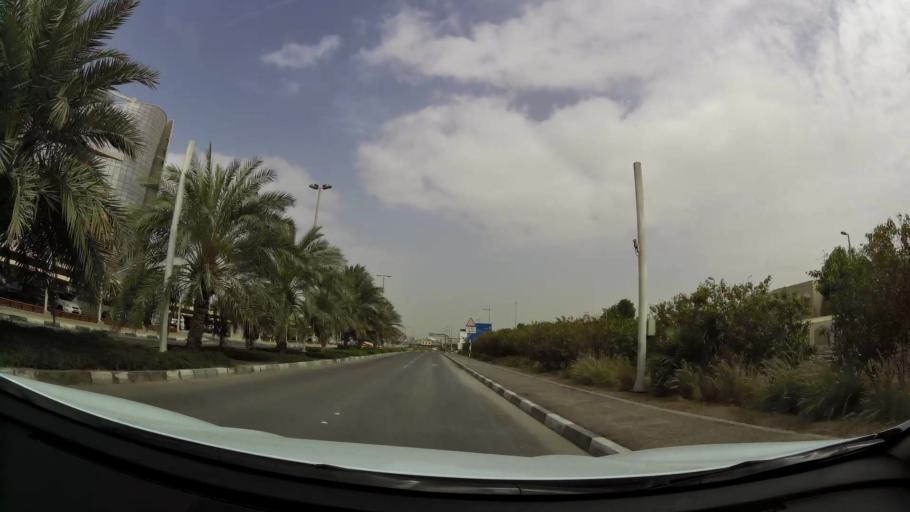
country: AE
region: Abu Dhabi
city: Abu Dhabi
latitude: 24.3962
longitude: 54.5017
